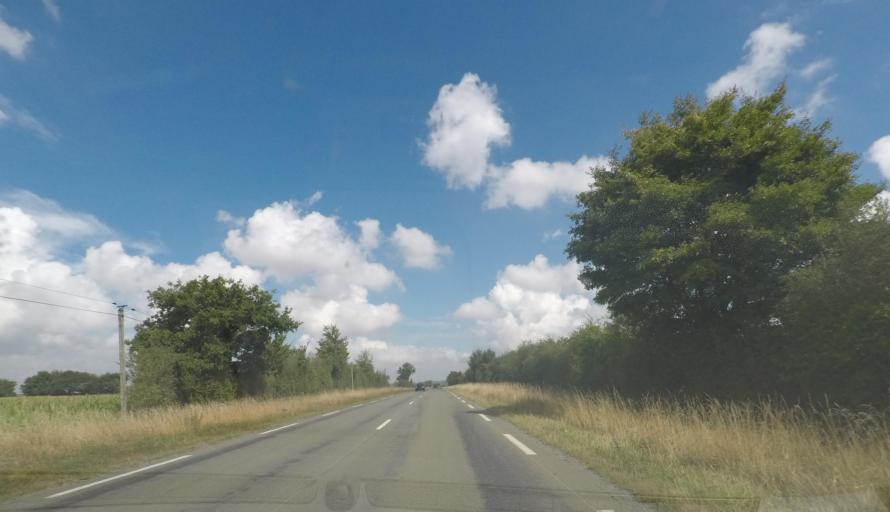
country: FR
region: Pays de la Loire
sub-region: Departement de la Sarthe
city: Saint-Cosme-en-Vairais
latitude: 48.2443
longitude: 0.4422
